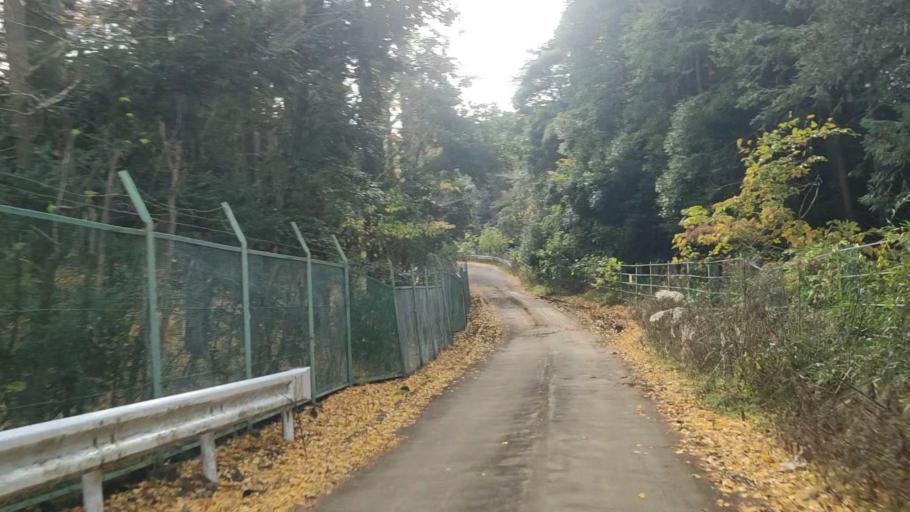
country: JP
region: Kanagawa
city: Minami-rinkan
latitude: 35.4832
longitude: 139.4995
